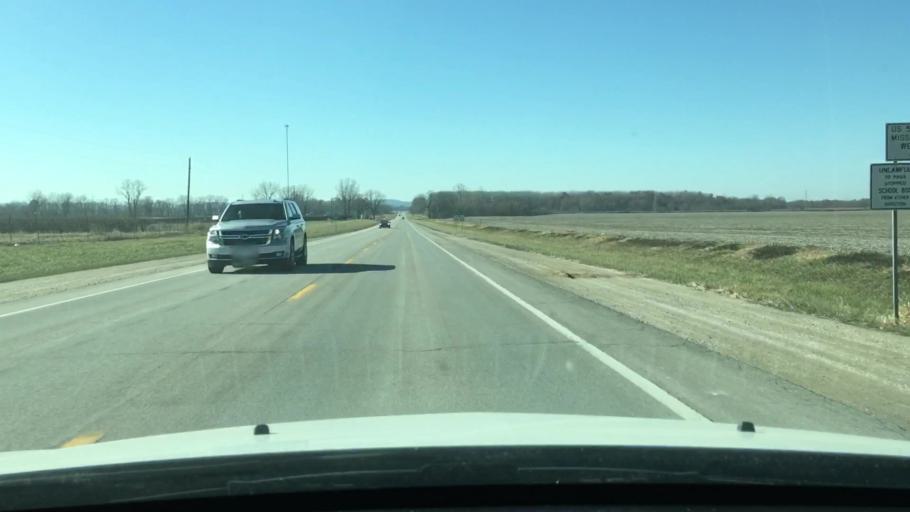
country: US
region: Missouri
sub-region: Pike County
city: Louisiana
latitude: 39.5123
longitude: -90.9716
